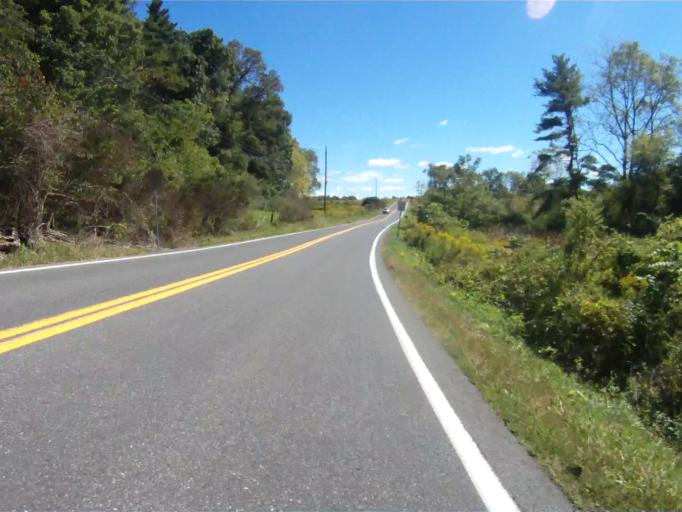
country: US
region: Pennsylvania
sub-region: Centre County
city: Park Forest Village
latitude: 40.8495
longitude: -77.8822
